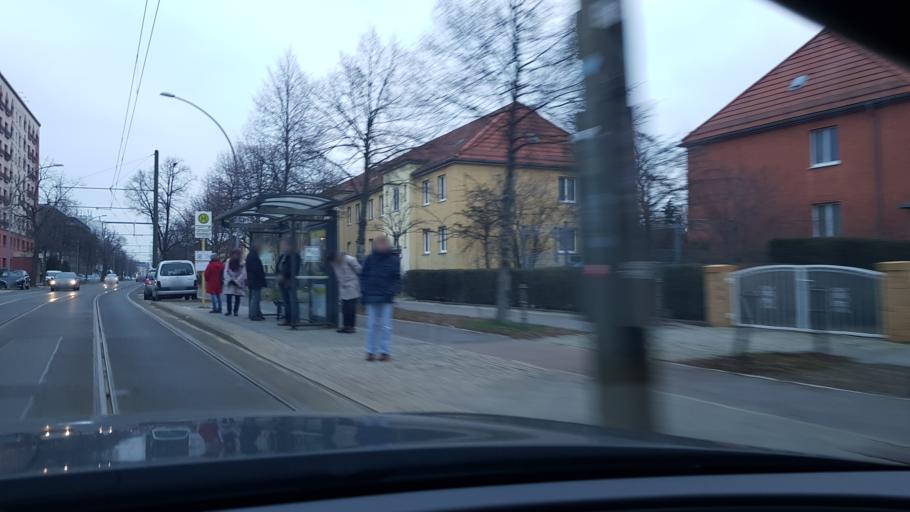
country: DE
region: Berlin
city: Berlin Koepenick
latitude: 52.4345
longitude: 13.5829
